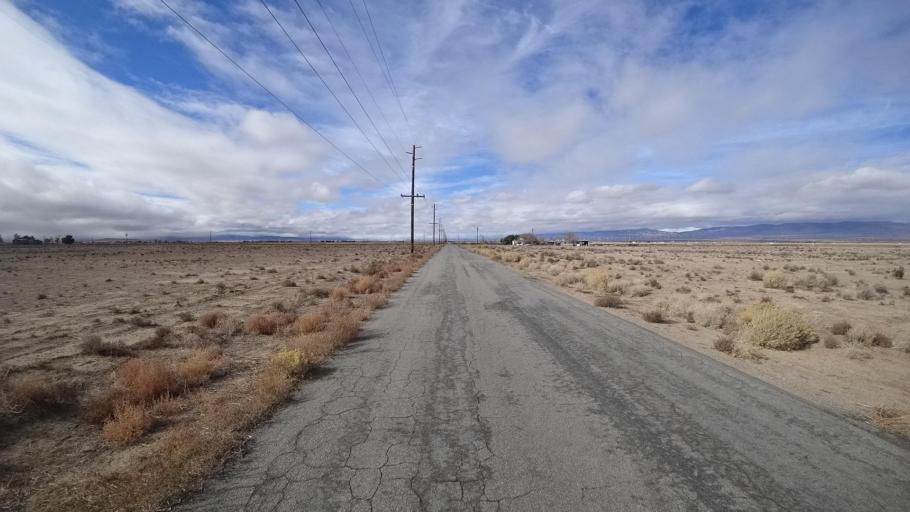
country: US
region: California
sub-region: Kern County
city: Rosamond
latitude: 34.8346
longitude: -118.2784
